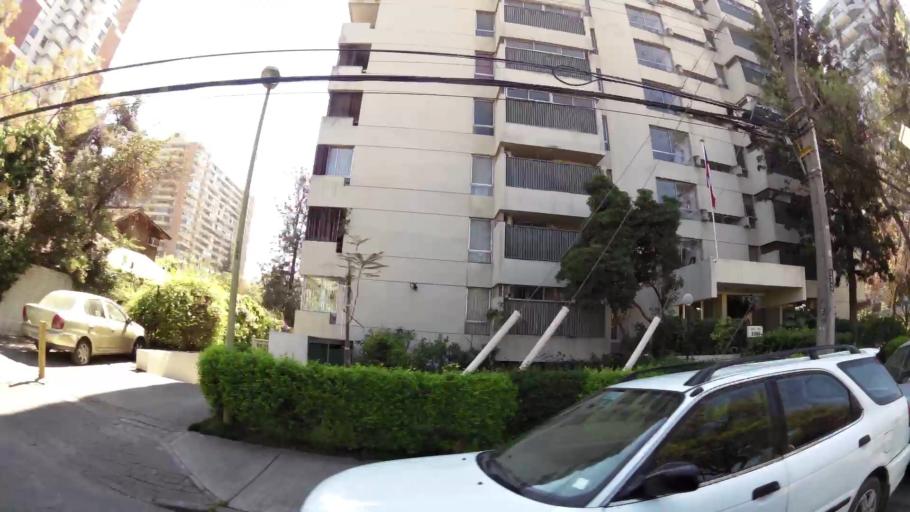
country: CL
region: Santiago Metropolitan
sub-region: Provincia de Santiago
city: Villa Presidente Frei, Nunoa, Santiago, Chile
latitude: -33.4201
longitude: -70.5695
